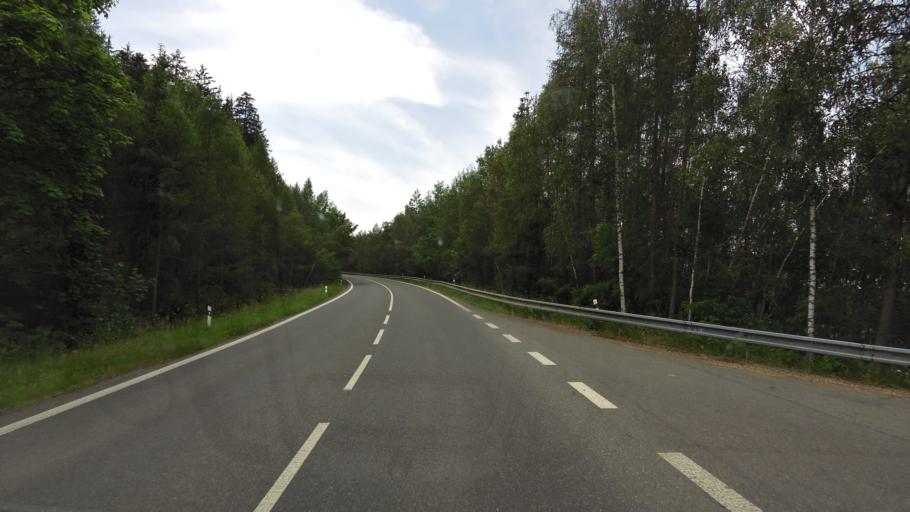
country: CZ
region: Plzensky
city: St'ahlavy
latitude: 49.6989
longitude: 13.5267
